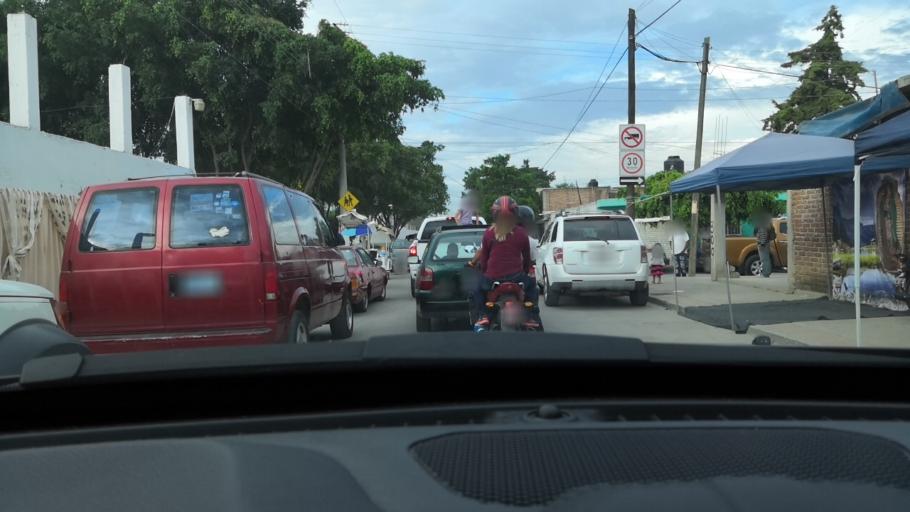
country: MX
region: Guanajuato
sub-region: Leon
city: Fraccionamiento Paraiso Real
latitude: 21.0946
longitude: -101.6039
